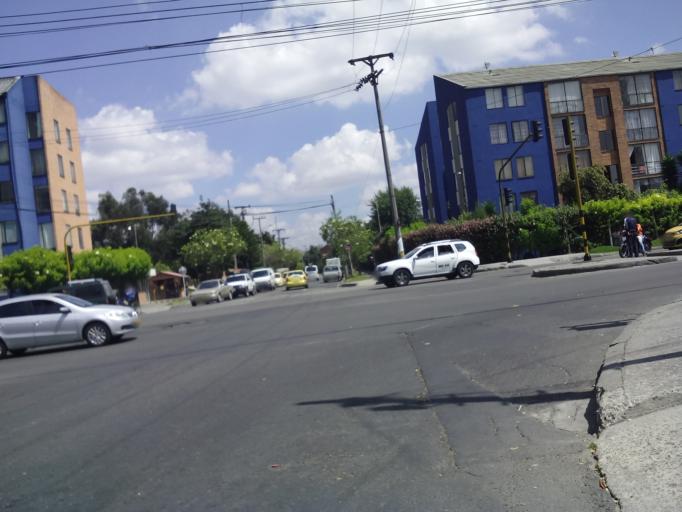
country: CO
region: Bogota D.C.
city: Bogota
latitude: 4.6798
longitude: -74.1328
